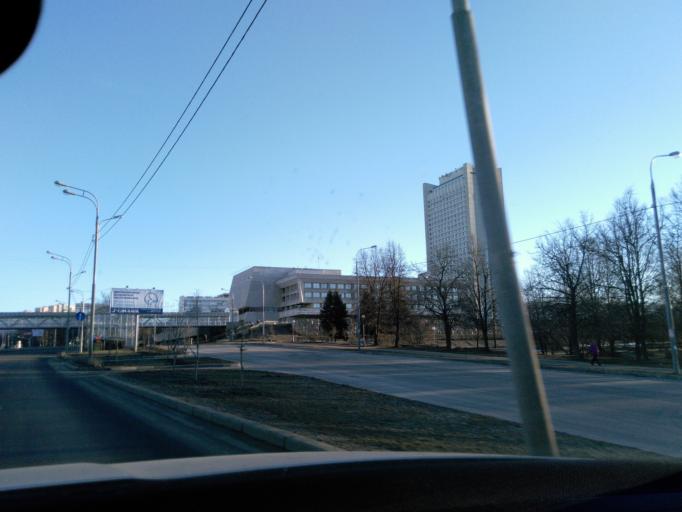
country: RU
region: Moscow
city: Zelenograd
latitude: 55.9890
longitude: 37.2130
